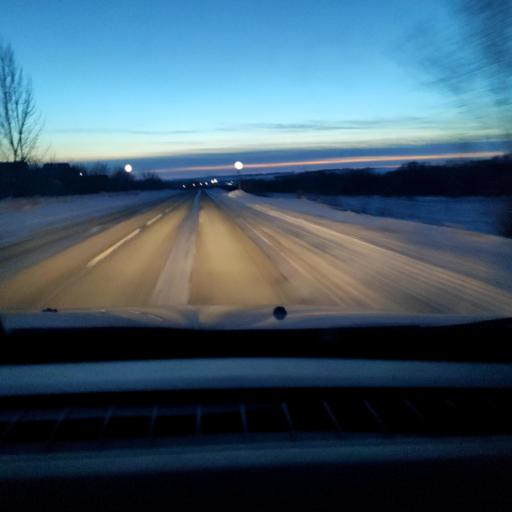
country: RU
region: Samara
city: Kinel'
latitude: 53.3012
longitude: 50.7804
